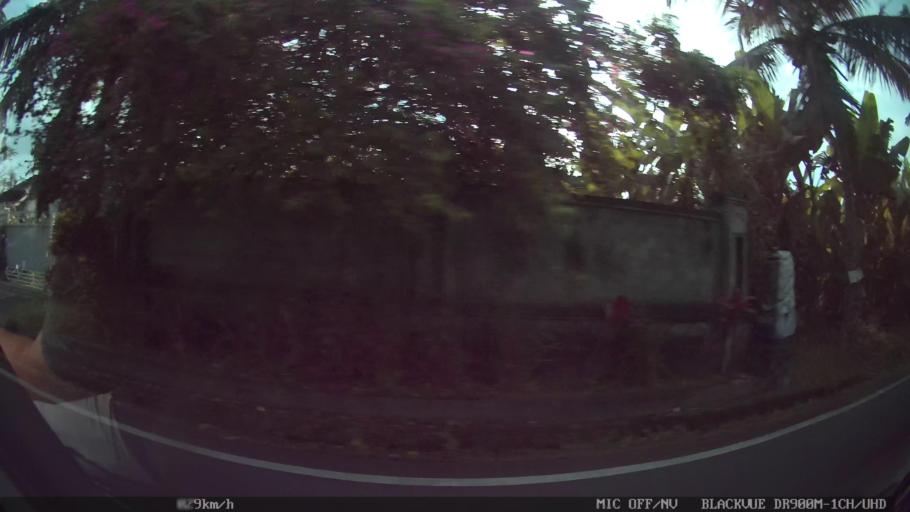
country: ID
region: Bali
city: Banjar Pande
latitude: -8.5168
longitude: 115.2501
